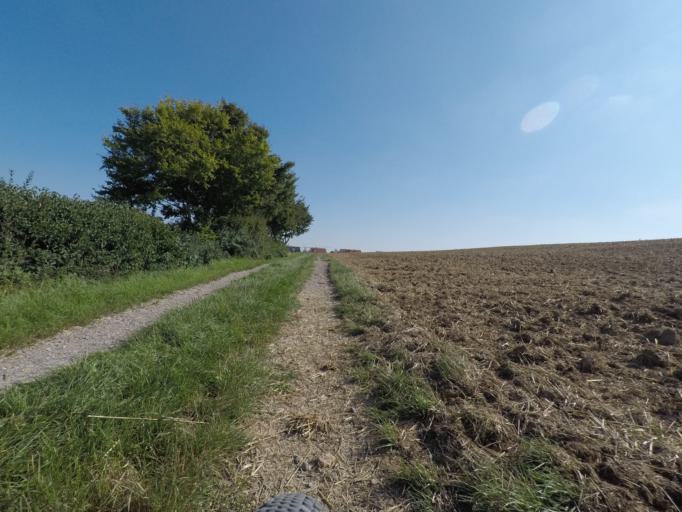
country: DE
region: Baden-Wuerttemberg
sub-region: Regierungsbezirk Stuttgart
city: Hildrizhausen
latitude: 48.6319
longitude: 8.9743
